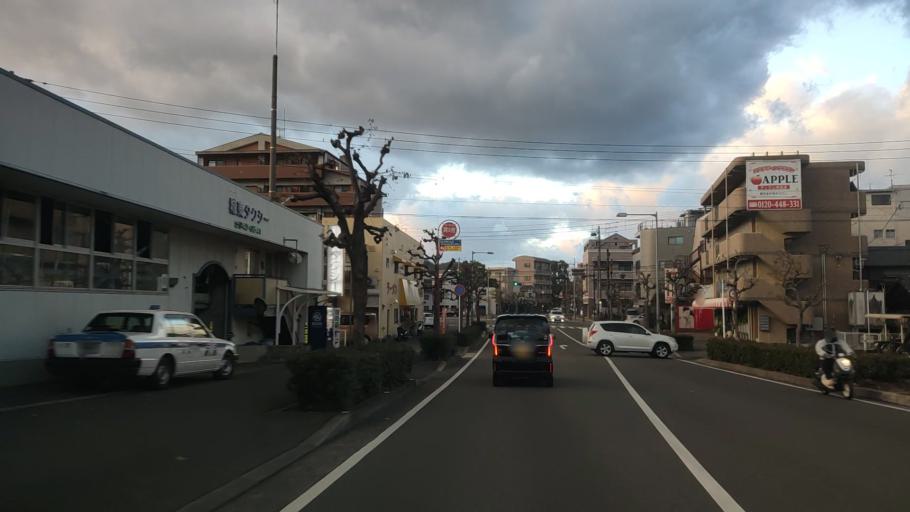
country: JP
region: Ehime
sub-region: Shikoku-chuo Shi
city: Matsuyama
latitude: 33.8406
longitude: 132.7852
